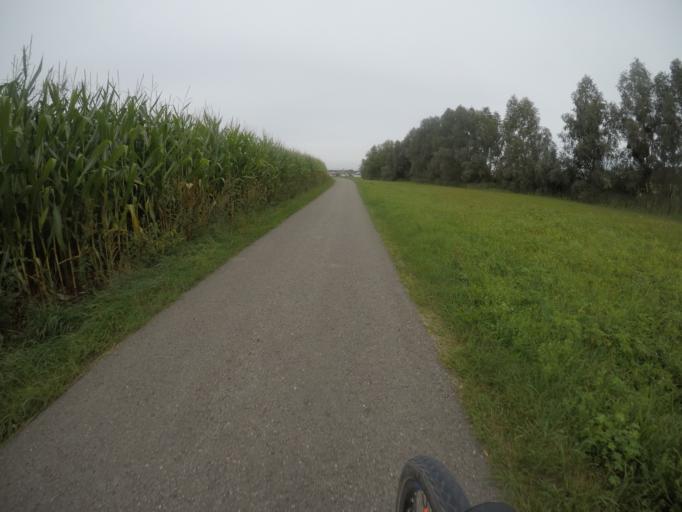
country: DE
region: Baden-Wuerttemberg
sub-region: Regierungsbezirk Stuttgart
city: Magstadt
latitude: 48.7429
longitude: 8.9827
